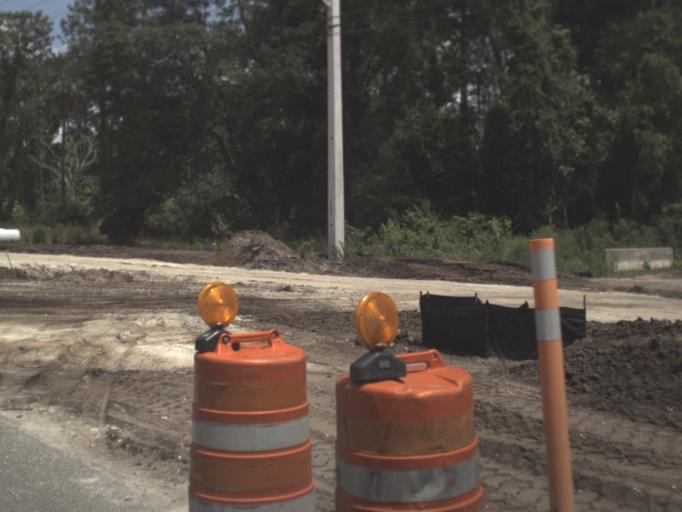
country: US
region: Florida
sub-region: Saint Johns County
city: Fruit Cove
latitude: 30.1391
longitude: -81.5138
